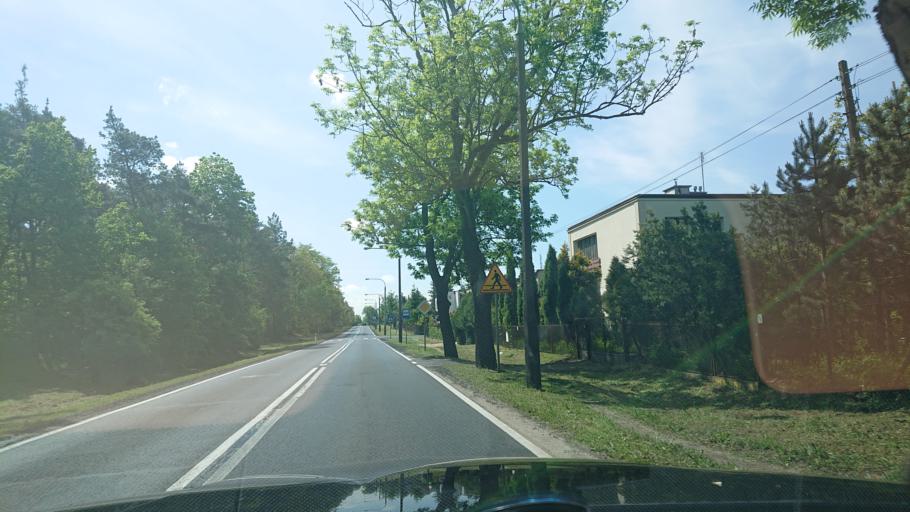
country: PL
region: Greater Poland Voivodeship
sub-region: Powiat gnieznienski
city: Gniezno
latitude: 52.5026
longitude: 17.5946
